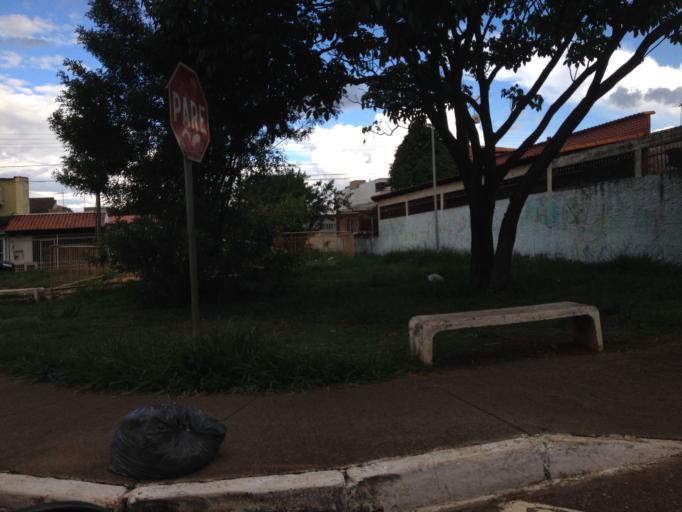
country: BR
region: Federal District
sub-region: Brasilia
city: Brasilia
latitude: -15.7887
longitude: -47.9388
